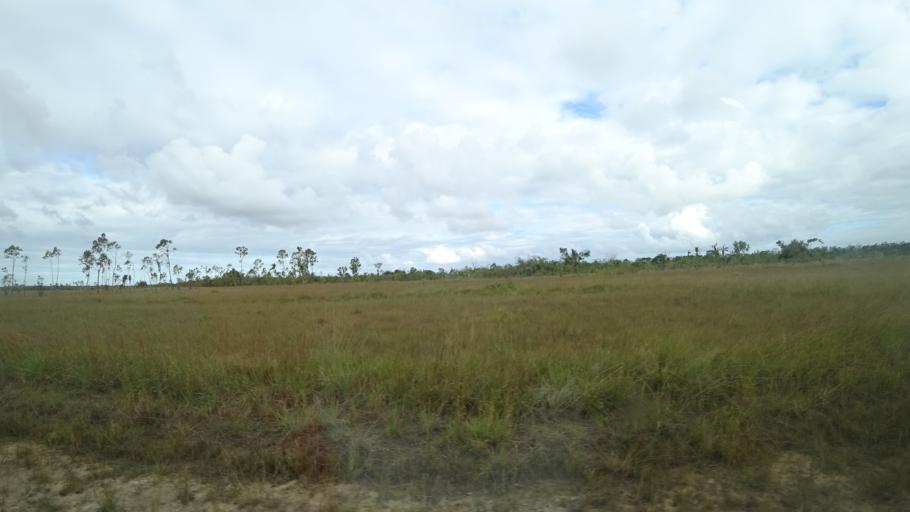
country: MZ
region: Sofala
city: Beira
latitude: -19.6150
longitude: 35.0656
